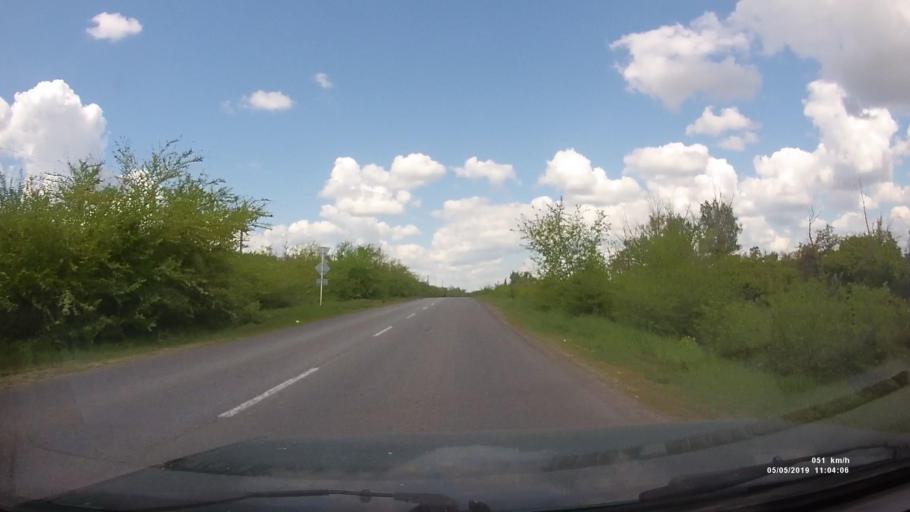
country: RU
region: Rostov
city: Ust'-Donetskiy
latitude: 47.6951
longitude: 40.9219
